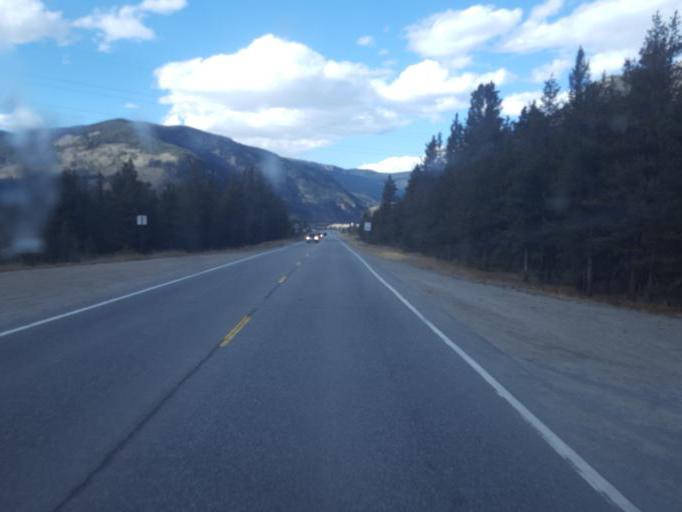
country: US
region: Colorado
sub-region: Summit County
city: Frisco
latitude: 39.4919
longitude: -106.1350
